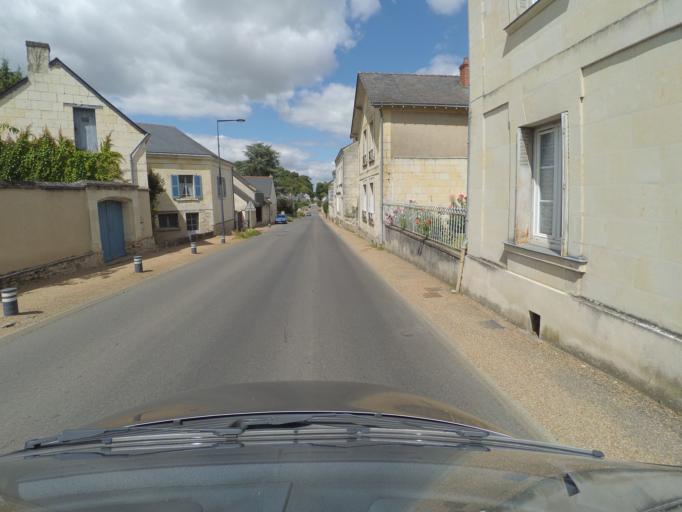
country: FR
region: Pays de la Loire
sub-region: Departement de Maine-et-Loire
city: Gennes
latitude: 47.3384
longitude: -0.2311
